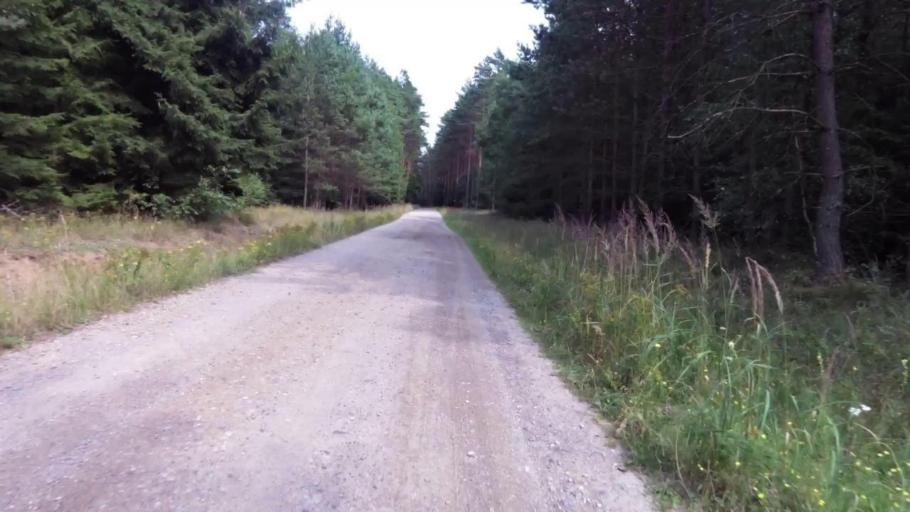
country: PL
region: West Pomeranian Voivodeship
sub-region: Powiat drawski
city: Zlocieniec
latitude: 53.5618
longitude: 15.9373
